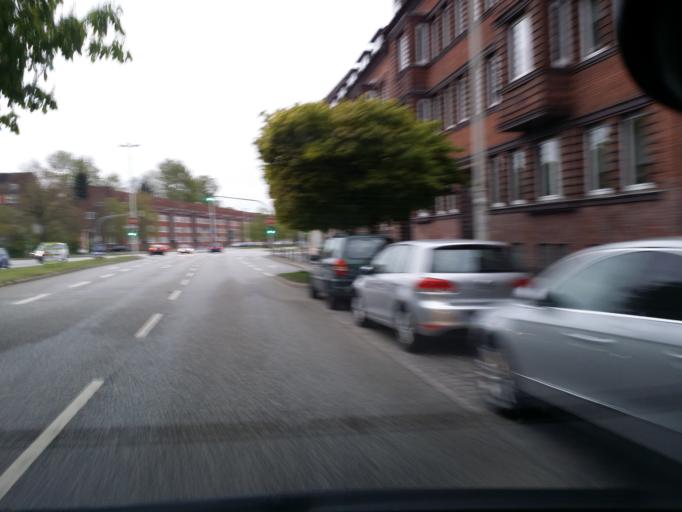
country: DE
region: Schleswig-Holstein
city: Kiel
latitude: 54.3327
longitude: 10.1224
